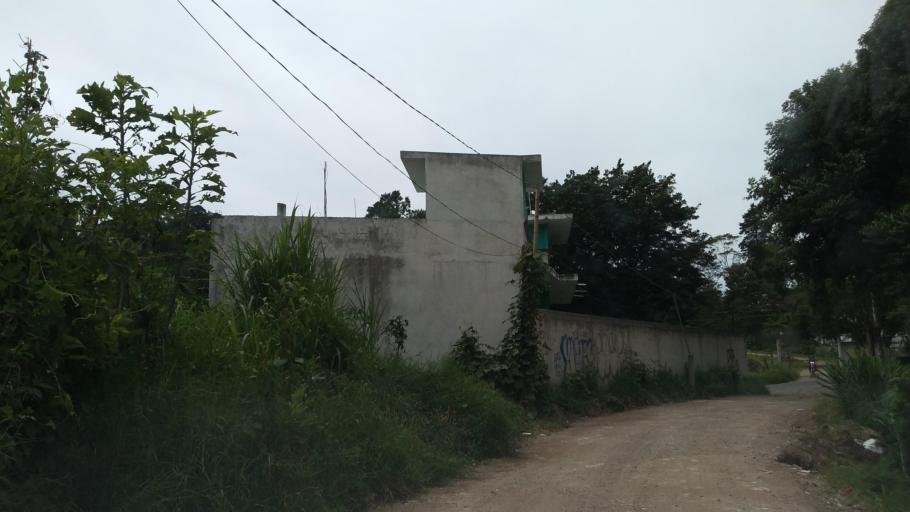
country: MX
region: Veracruz
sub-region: Tlalnelhuayocan
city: Guadalupe Victoria
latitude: 19.5501
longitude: -96.9575
